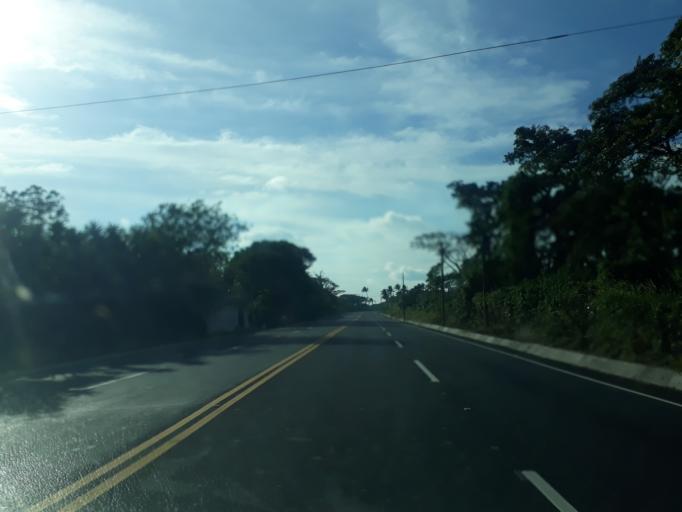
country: NI
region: Carazo
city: Diriamba
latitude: 11.9164
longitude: -86.2729
